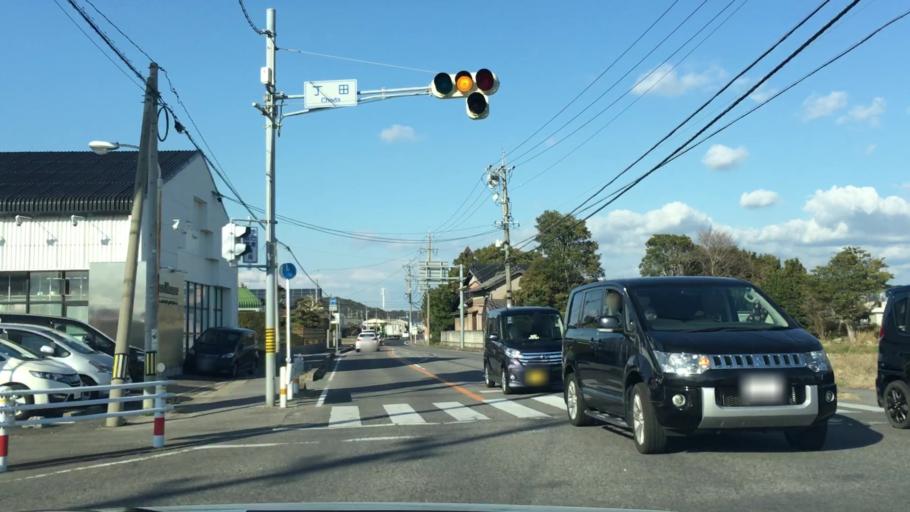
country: JP
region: Aichi
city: Nishio
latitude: 34.8604
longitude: 137.0688
